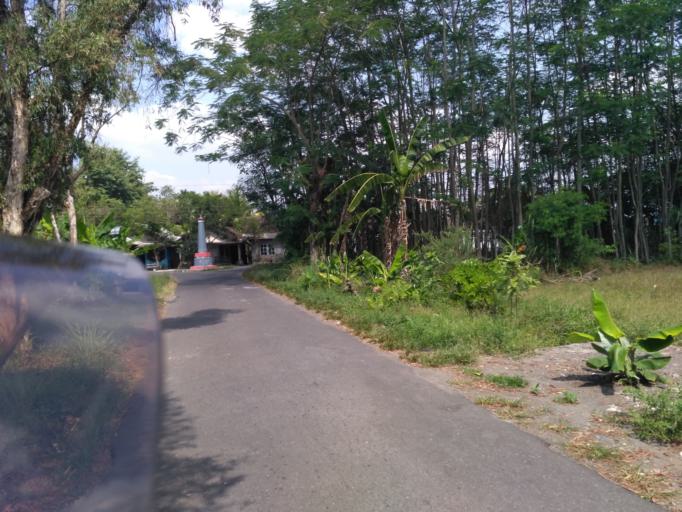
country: ID
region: Daerah Istimewa Yogyakarta
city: Depok
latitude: -7.7186
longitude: 110.4237
